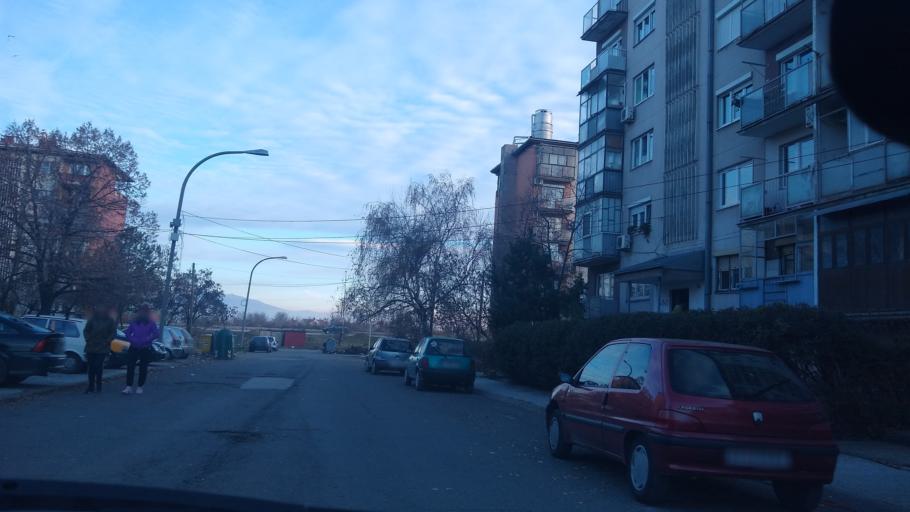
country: MK
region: Bitola
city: Bitola
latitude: 41.0273
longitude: 21.3443
